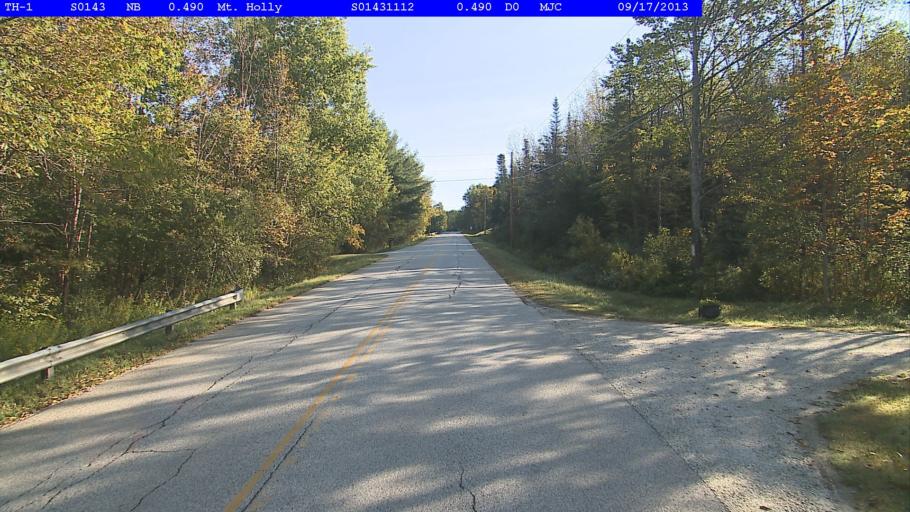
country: US
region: Vermont
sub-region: Rutland County
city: Rutland
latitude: 43.4118
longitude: -72.8319
